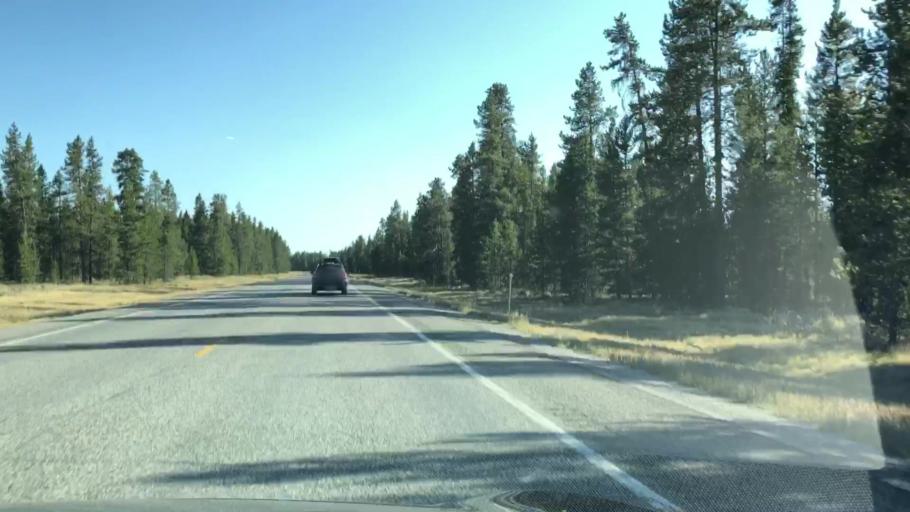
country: US
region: Montana
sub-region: Gallatin County
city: West Yellowstone
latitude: 44.7439
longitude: -111.1133
